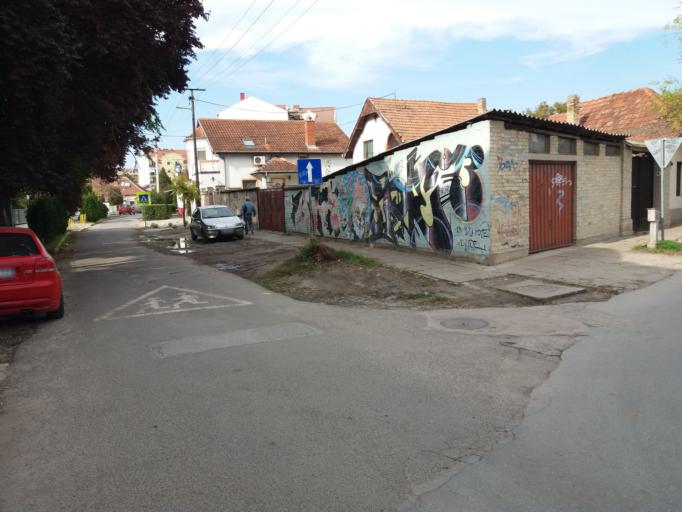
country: RS
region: Autonomna Pokrajina Vojvodina
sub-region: Severnobacki Okrug
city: Subotica
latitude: 46.1049
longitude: 19.6665
